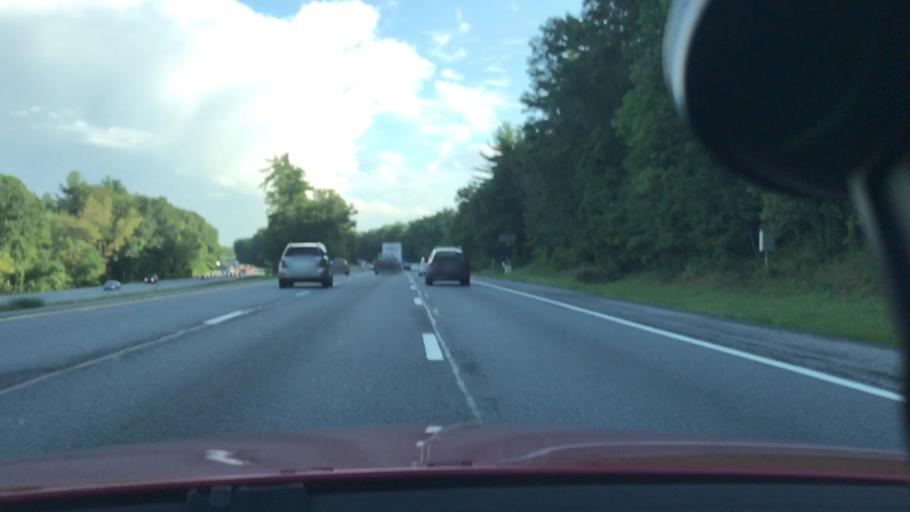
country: US
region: New York
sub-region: Albany County
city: Cohoes
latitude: 42.8305
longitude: -73.7701
